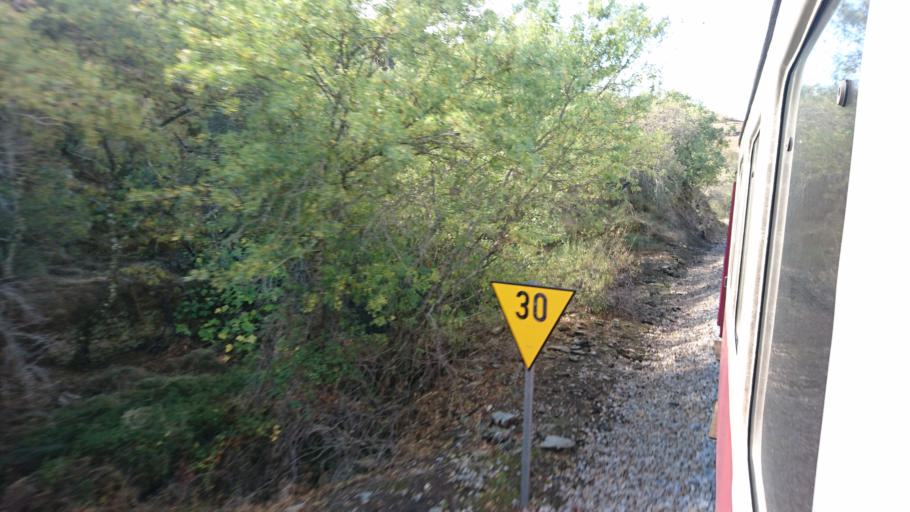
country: PT
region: Guarda
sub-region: Vila Nova de Foz Coa
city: Custoias
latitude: 41.1423
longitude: -7.2590
